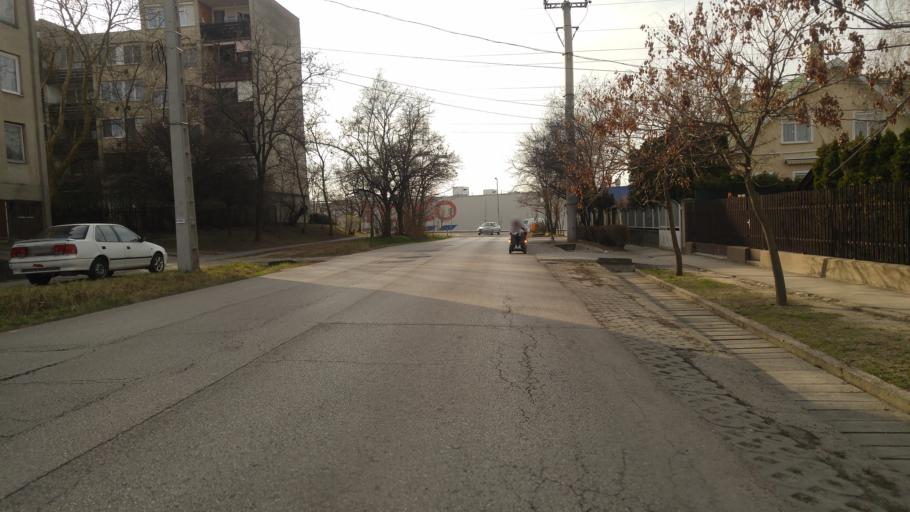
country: HU
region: Budapest
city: Budapest XVII. keruelet
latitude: 47.4823
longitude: 19.2305
